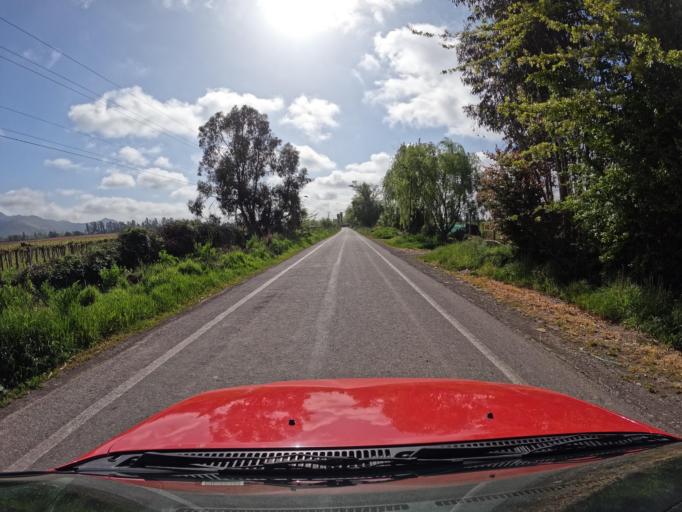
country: CL
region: Maule
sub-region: Provincia de Curico
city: Teno
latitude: -34.8799
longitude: -71.2359
